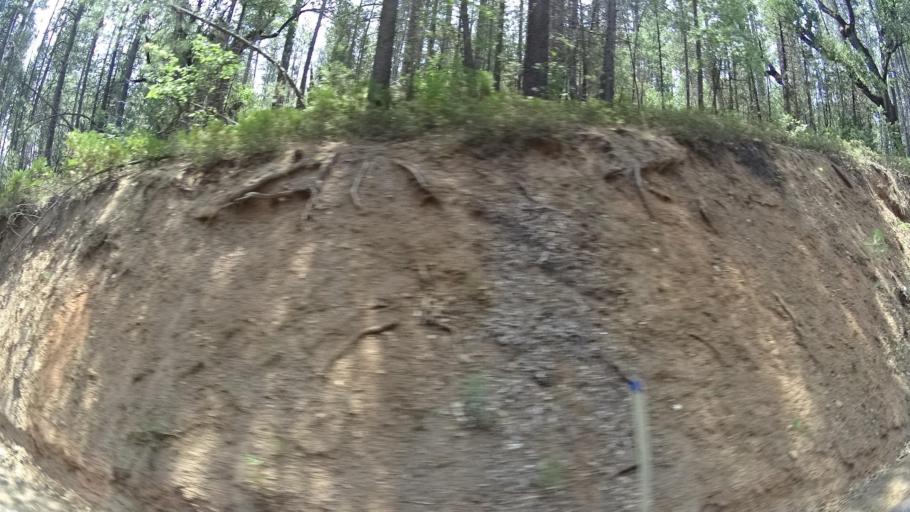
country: US
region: California
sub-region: Tuolumne County
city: Tuolumne City
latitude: 37.7549
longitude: -120.1140
